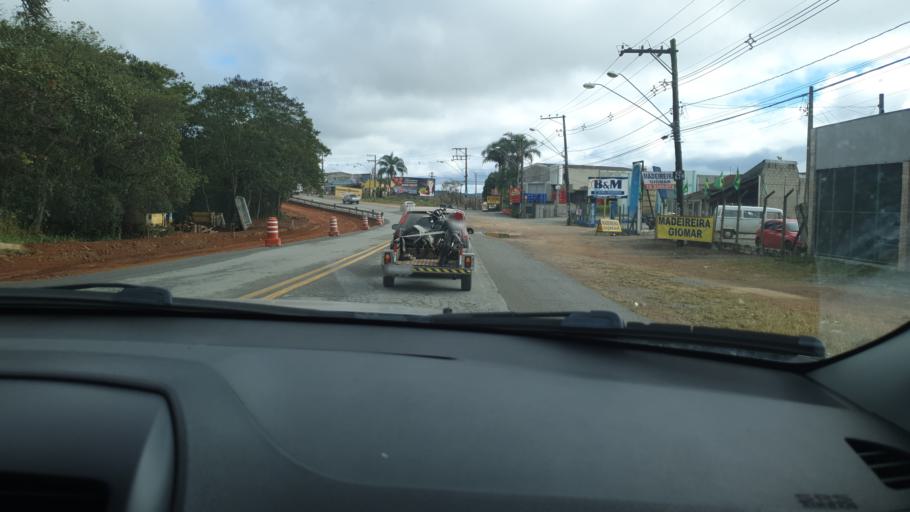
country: BR
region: Sao Paulo
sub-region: Ibiuna
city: Ibiuna
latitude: -23.6595
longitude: -47.1966
